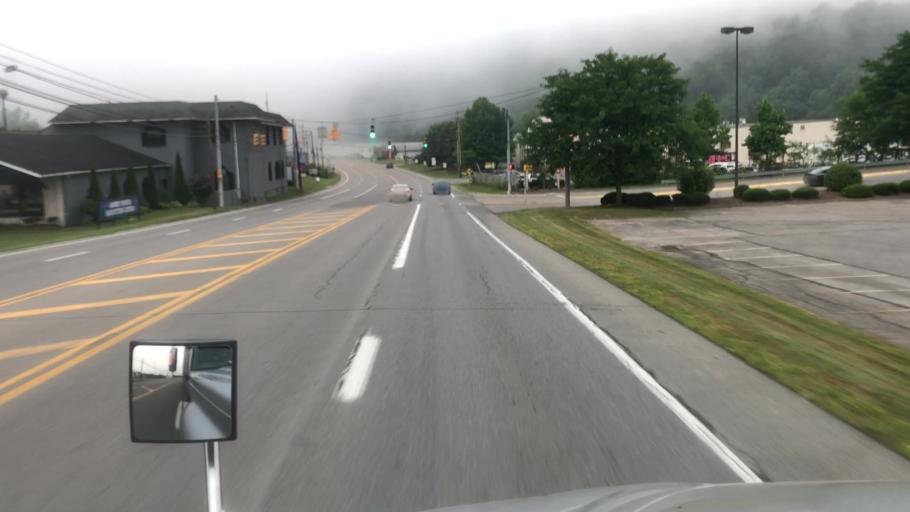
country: US
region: Pennsylvania
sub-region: Venango County
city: Franklin
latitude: 41.4018
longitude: -79.8099
